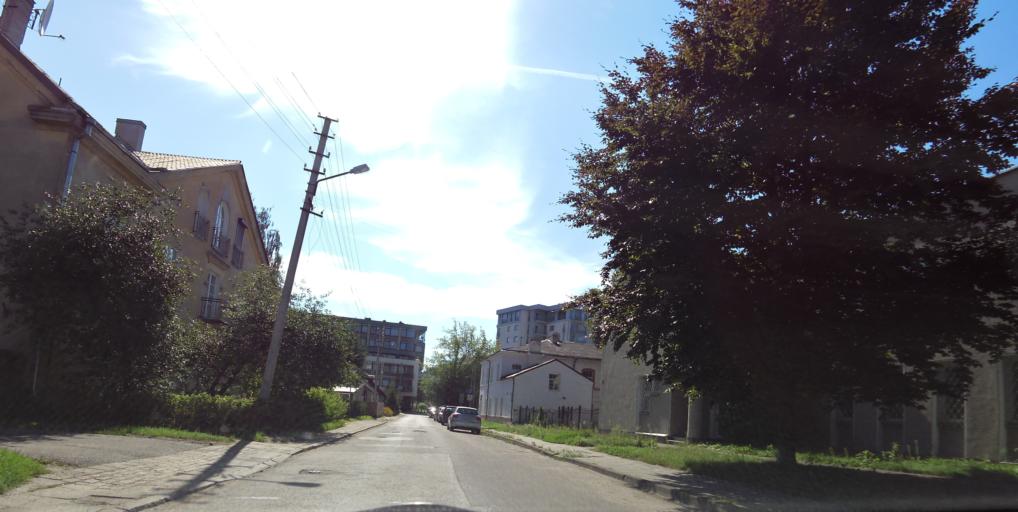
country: LT
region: Vilnius County
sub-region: Vilnius
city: Vilnius
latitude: 54.6945
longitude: 25.2947
